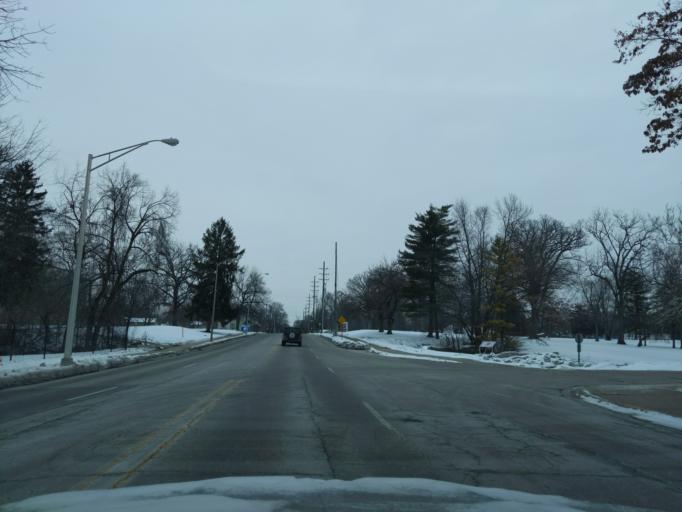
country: US
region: Indiana
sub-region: Tippecanoe County
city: Lafayette
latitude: 40.3998
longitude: -86.8767
